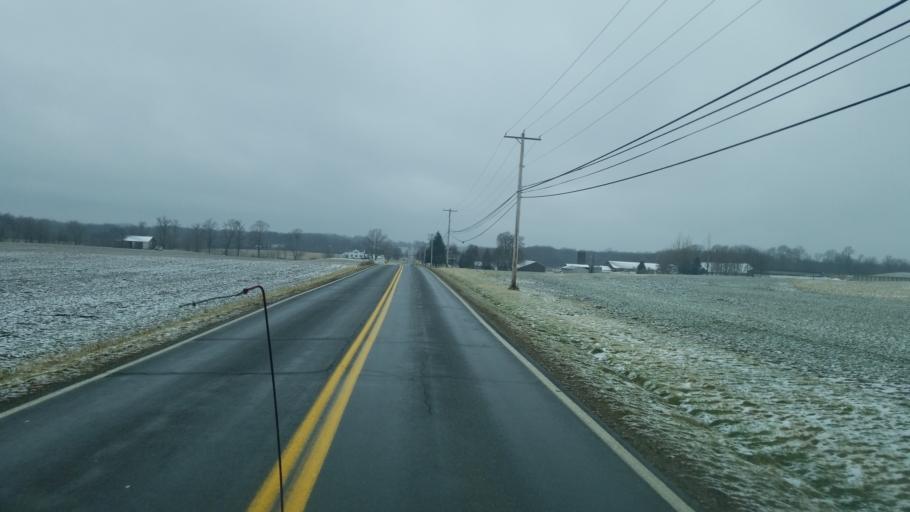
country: US
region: Ohio
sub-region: Portage County
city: Mantua
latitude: 41.2841
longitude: -81.2641
